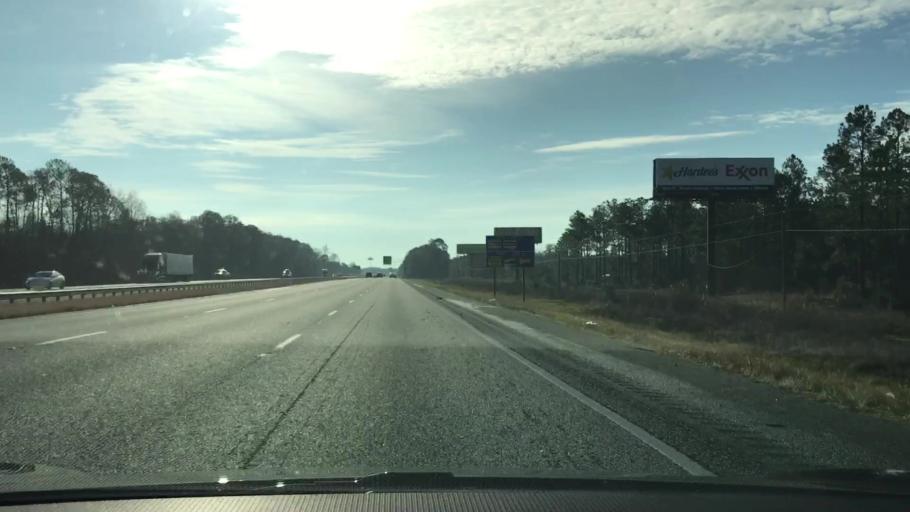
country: US
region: Georgia
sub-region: Lowndes County
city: Valdosta
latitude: 30.7673
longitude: -83.2883
